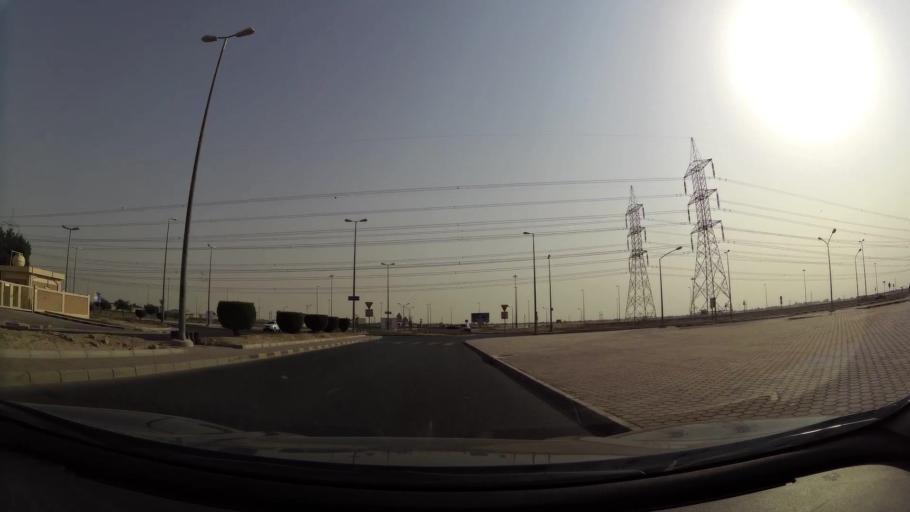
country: KW
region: Al Asimah
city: Ar Rabiyah
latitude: 29.2980
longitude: 47.8009
